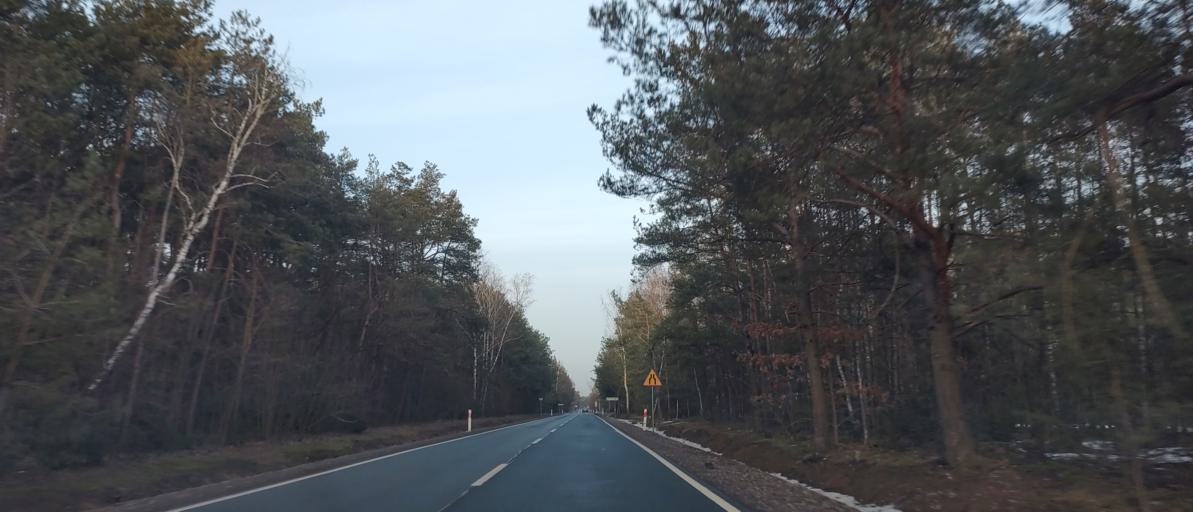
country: PL
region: Masovian Voivodeship
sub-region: Powiat bialobrzeski
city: Bialobrzegi
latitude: 51.6398
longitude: 20.9129
